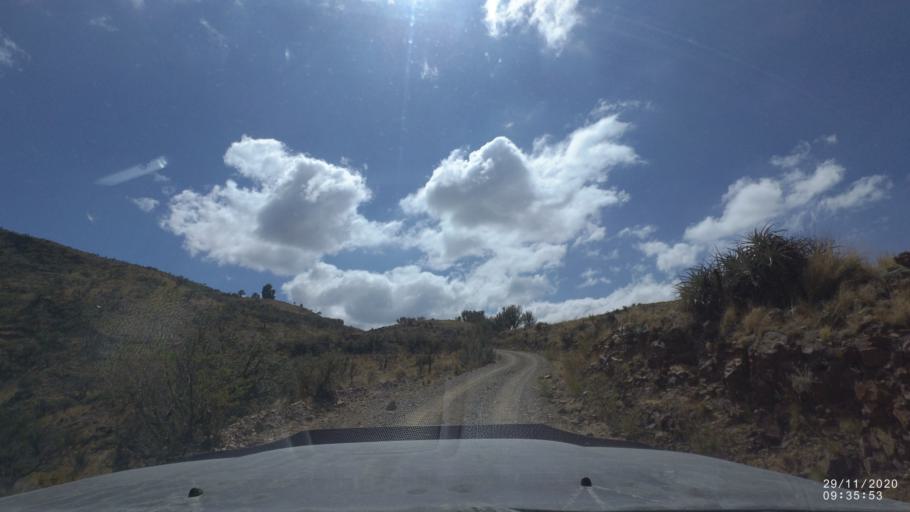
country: BO
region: Cochabamba
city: Cochabamba
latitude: -17.3093
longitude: -66.1895
